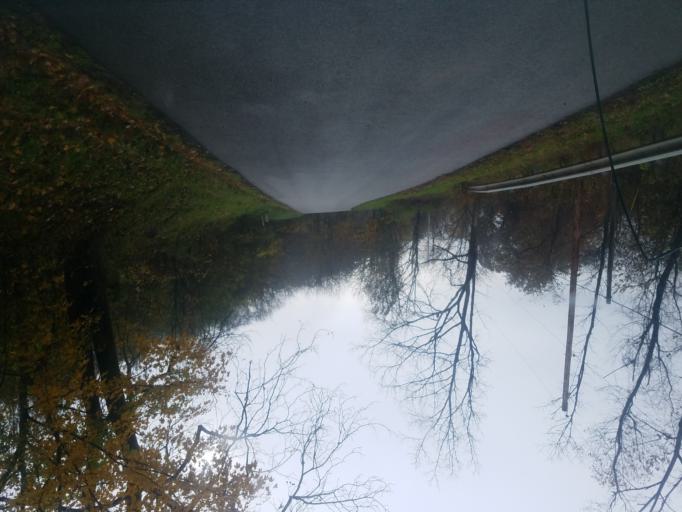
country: US
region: Ohio
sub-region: Morgan County
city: McConnelsville
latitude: 39.5421
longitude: -81.7927
